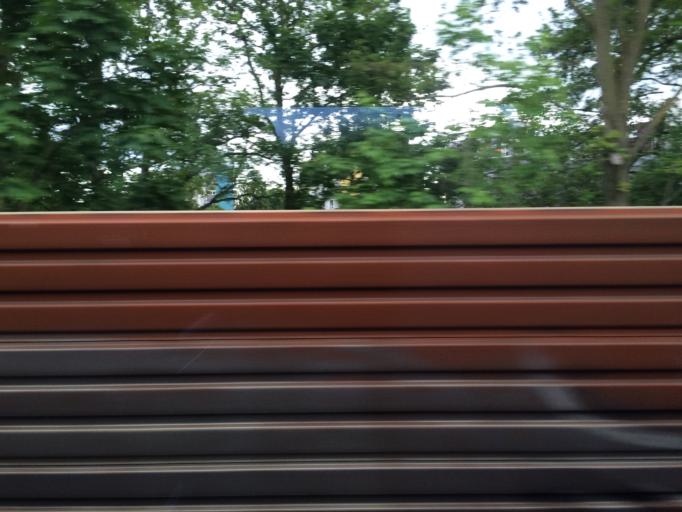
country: DE
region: Hesse
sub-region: Regierungsbezirk Darmstadt
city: Frankfurt am Main
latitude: 50.0925
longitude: 8.6618
